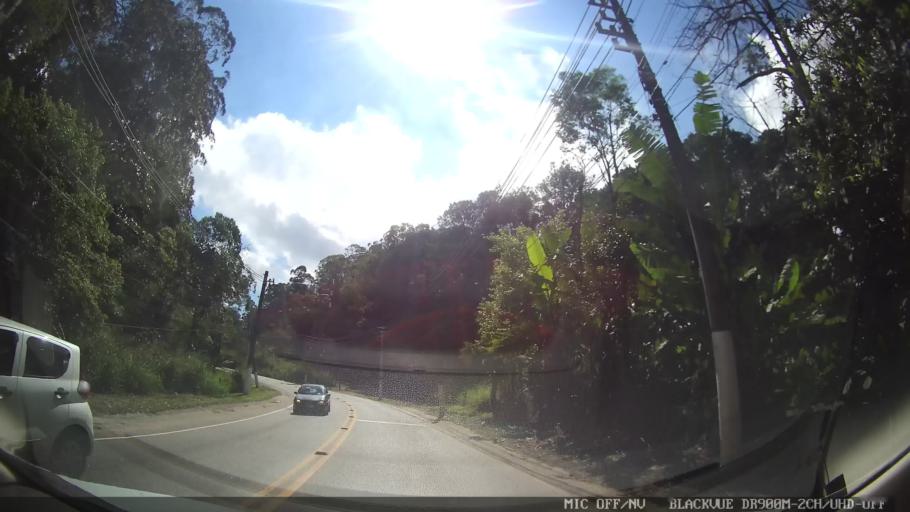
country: BR
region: Sao Paulo
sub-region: Caieiras
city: Caieiras
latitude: -23.4208
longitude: -46.7850
